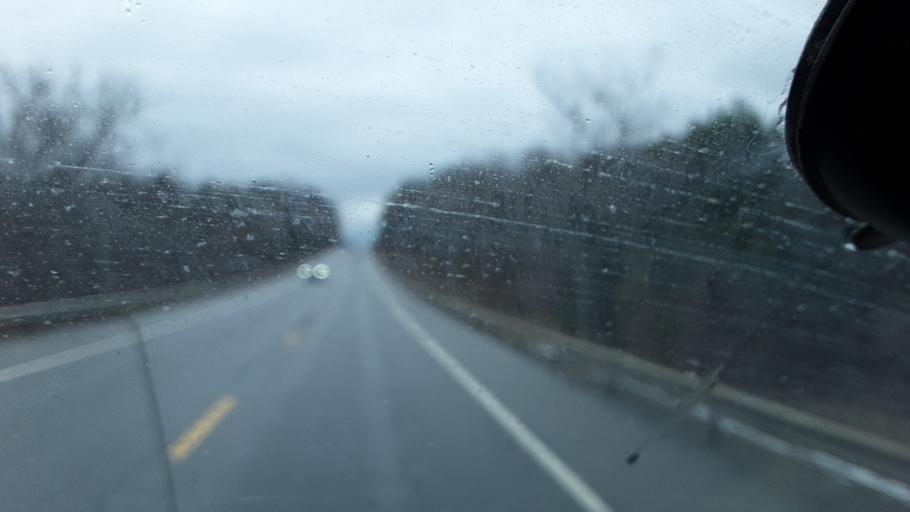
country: US
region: New York
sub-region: Erie County
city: Holland
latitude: 42.6042
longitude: -78.4997
